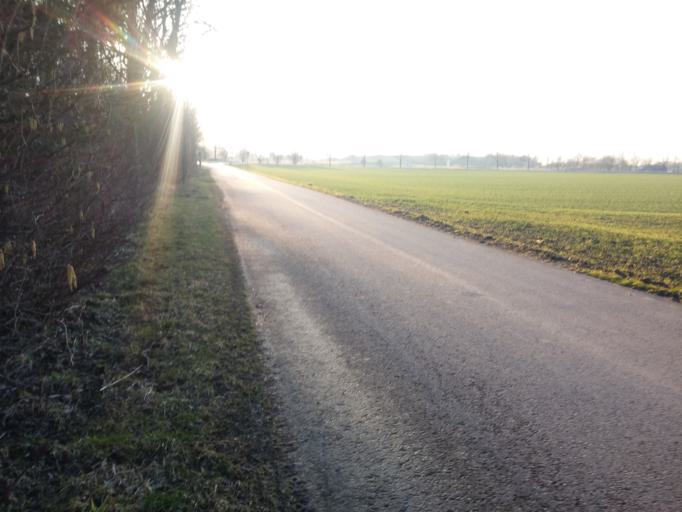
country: DE
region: Bavaria
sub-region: Upper Bavaria
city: Aschheim
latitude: 48.1815
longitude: 11.7123
